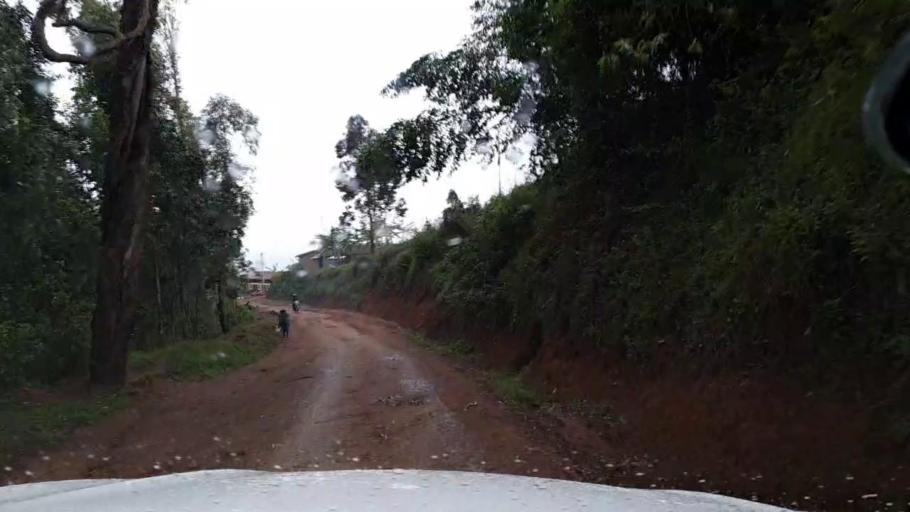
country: BI
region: Kayanza
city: Kayanza
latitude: -2.7820
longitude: 29.5344
